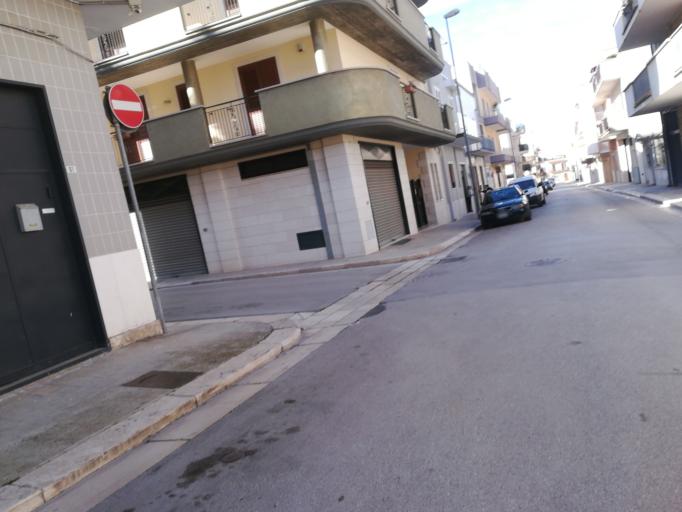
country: IT
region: Apulia
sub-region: Provincia di Barletta - Andria - Trani
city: Andria
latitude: 41.2198
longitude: 16.3043
